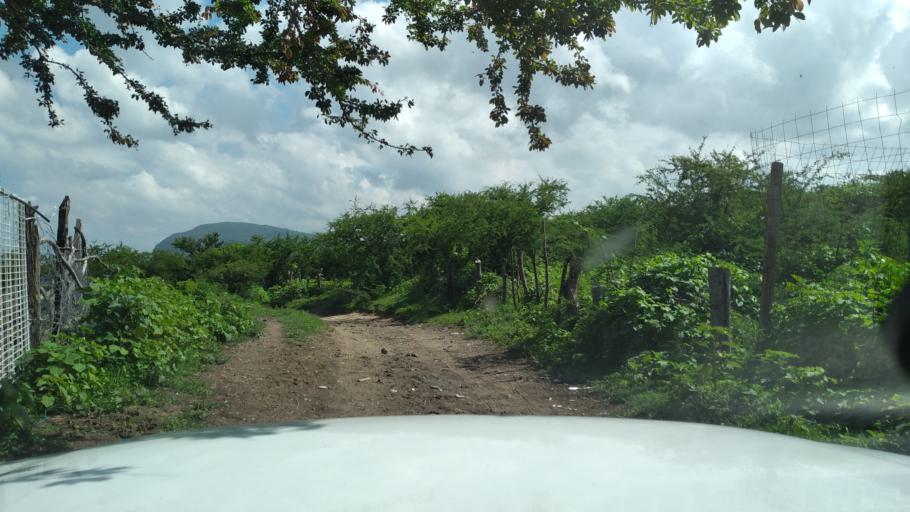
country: MX
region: Jalisco
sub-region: Zapopan
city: San Isidro
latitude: 20.7309
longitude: -103.2974
